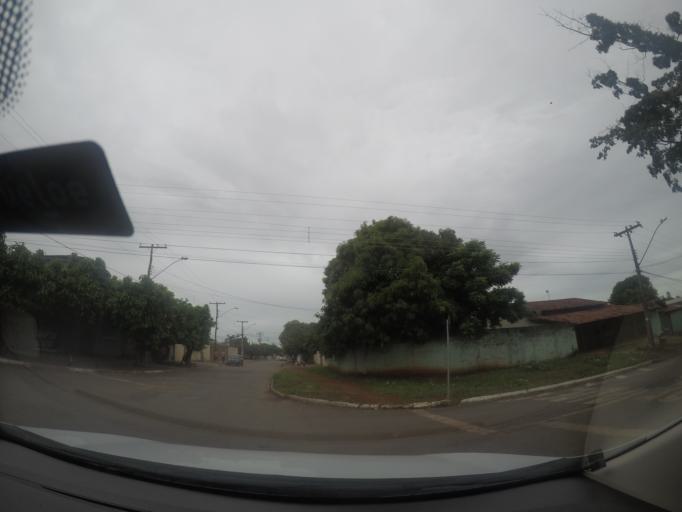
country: BR
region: Goias
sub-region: Goiania
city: Goiania
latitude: -16.6706
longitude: -49.3229
